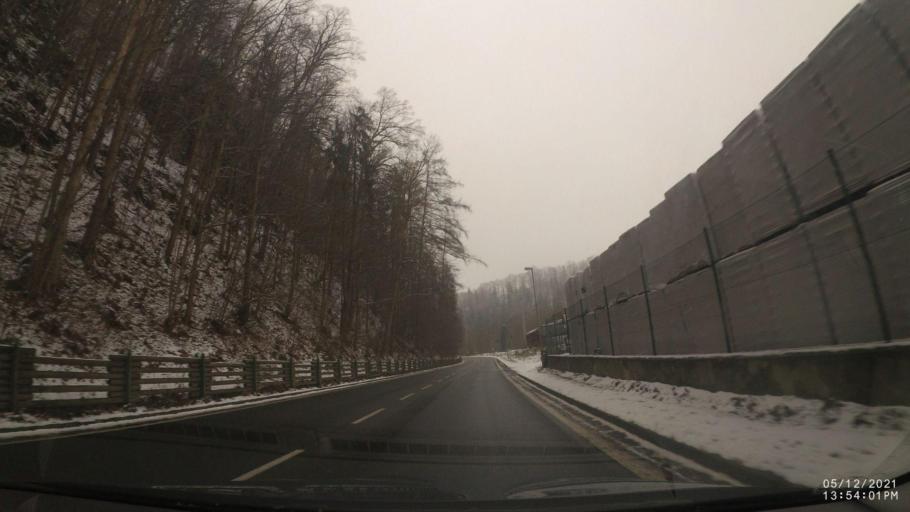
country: CZ
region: Kralovehradecky
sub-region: Okres Nachod
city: Police nad Metuji
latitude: 50.5119
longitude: 16.2133
